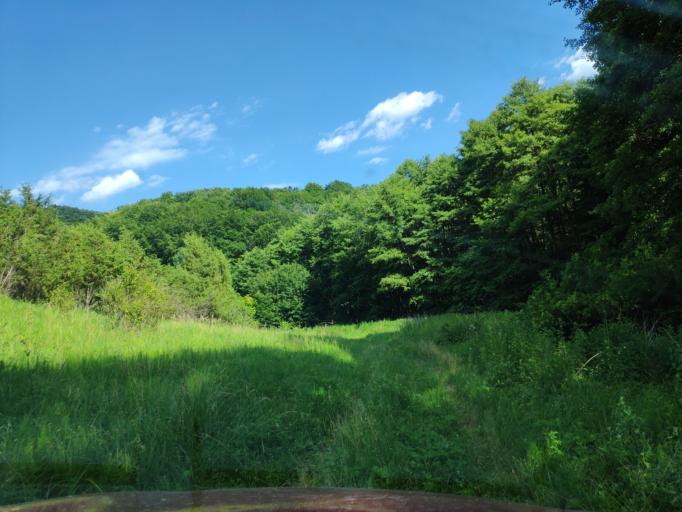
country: HU
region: Borsod-Abauj-Zemplen
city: Arlo
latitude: 48.2557
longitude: 20.1265
